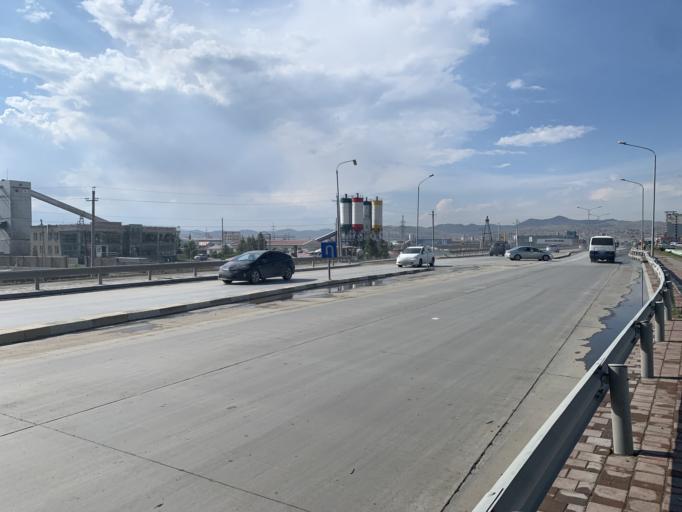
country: MN
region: Ulaanbaatar
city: Ulaanbaatar
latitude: 47.8844
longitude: 106.7852
